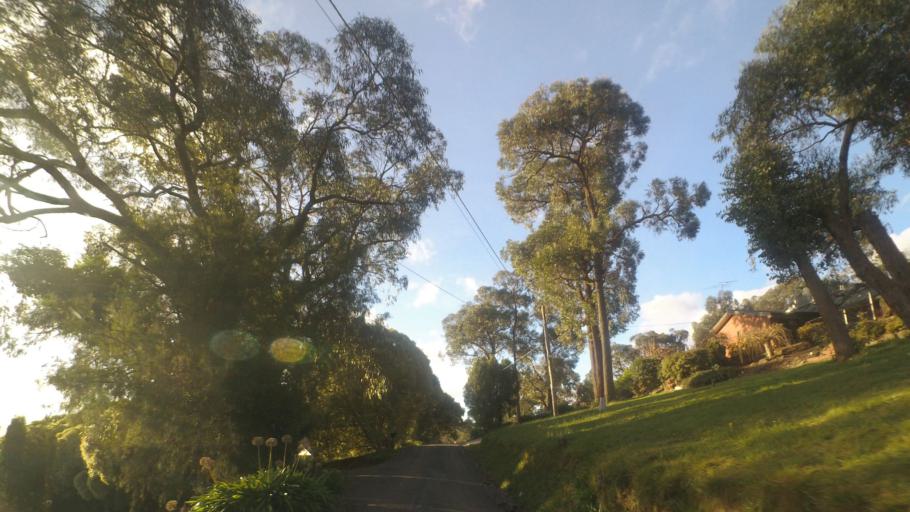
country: AU
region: Victoria
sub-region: Yarra Ranges
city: Kalorama
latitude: -37.8103
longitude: 145.3646
